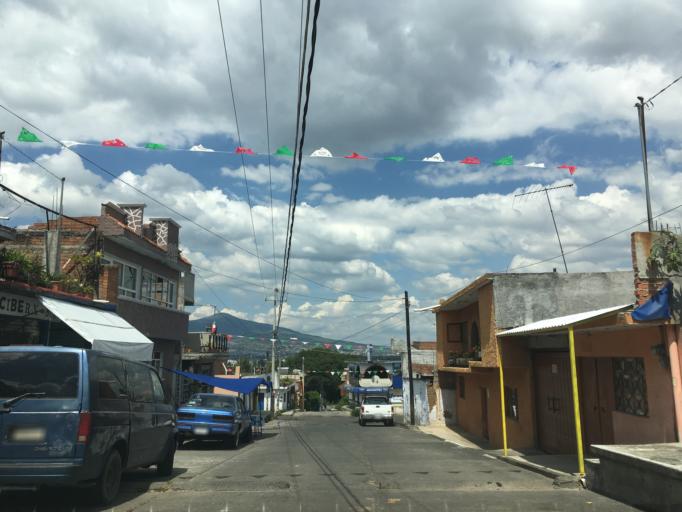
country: MX
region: Michoacan
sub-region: Morelia
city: Morelos
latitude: 19.6518
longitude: -101.2368
